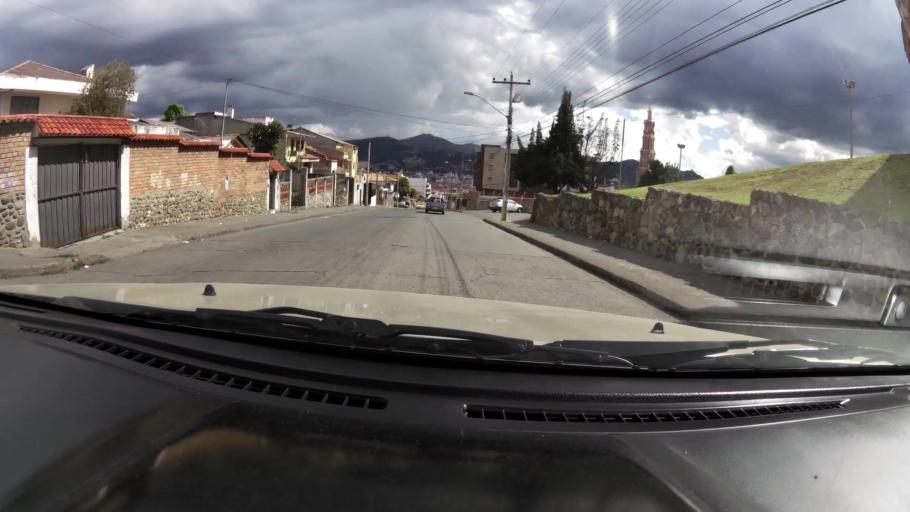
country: EC
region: Azuay
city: Cuenca
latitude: -2.8866
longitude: -79.0023
